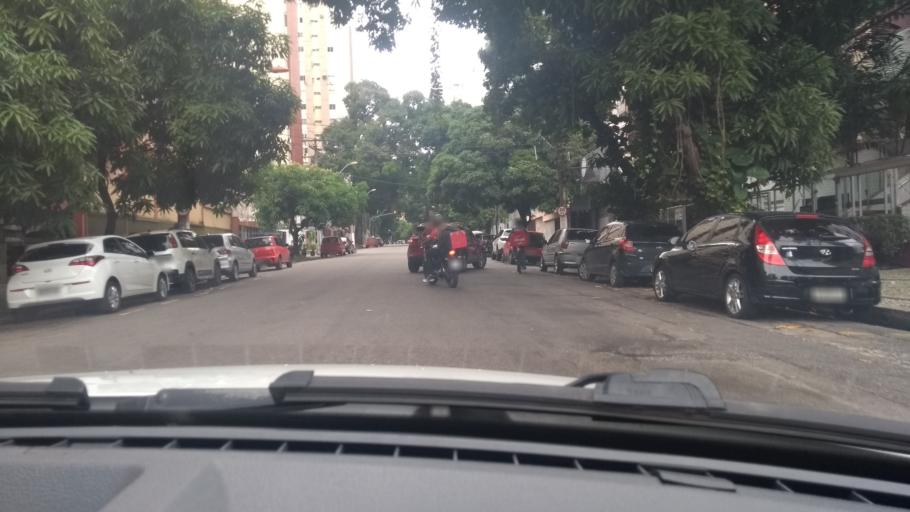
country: BR
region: Para
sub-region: Belem
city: Belem
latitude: -1.4624
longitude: -48.4926
